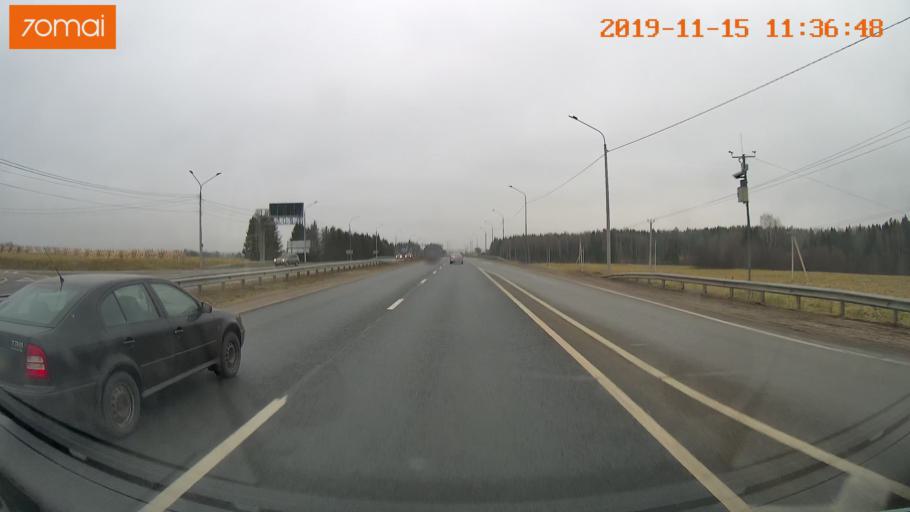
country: RU
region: Vologda
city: Molochnoye
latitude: 59.2023
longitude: 39.6566
